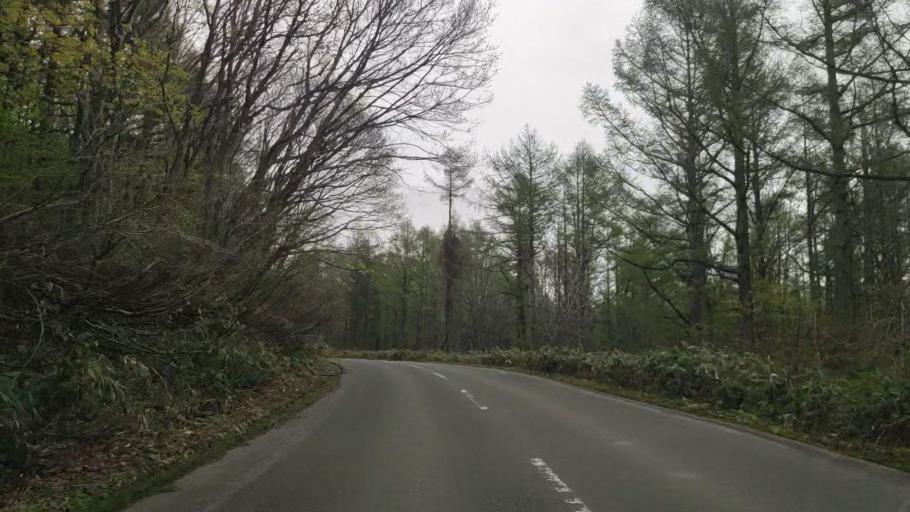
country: JP
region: Aomori
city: Aomori Shi
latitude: 40.7317
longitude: 140.8413
